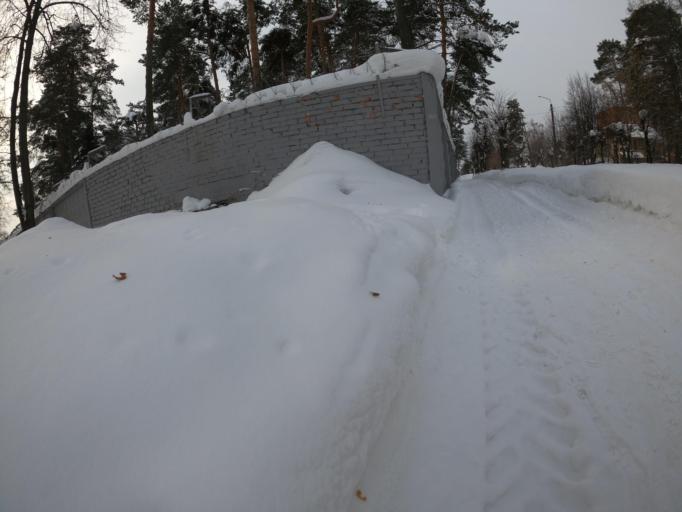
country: RU
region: Moskovskaya
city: Elektrogorsk
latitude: 55.8893
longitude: 38.7782
